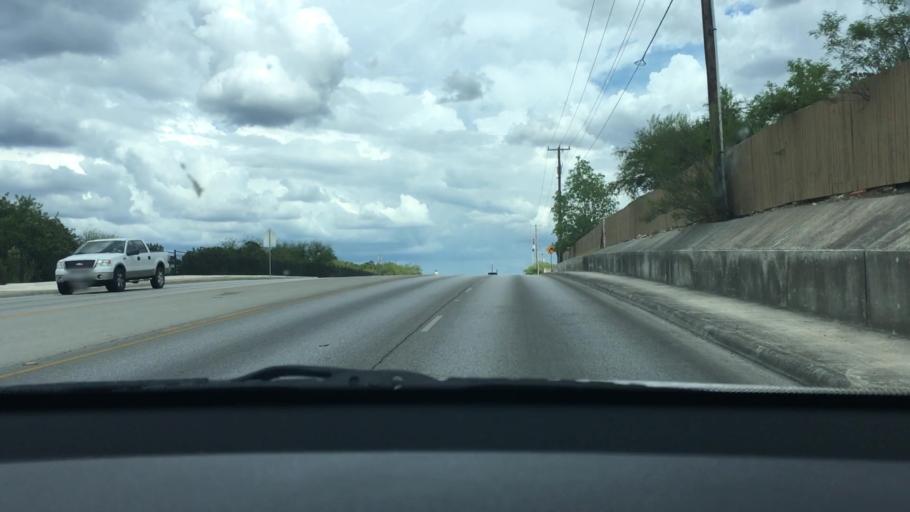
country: US
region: Texas
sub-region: Bexar County
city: Timberwood Park
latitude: 29.6548
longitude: -98.4299
